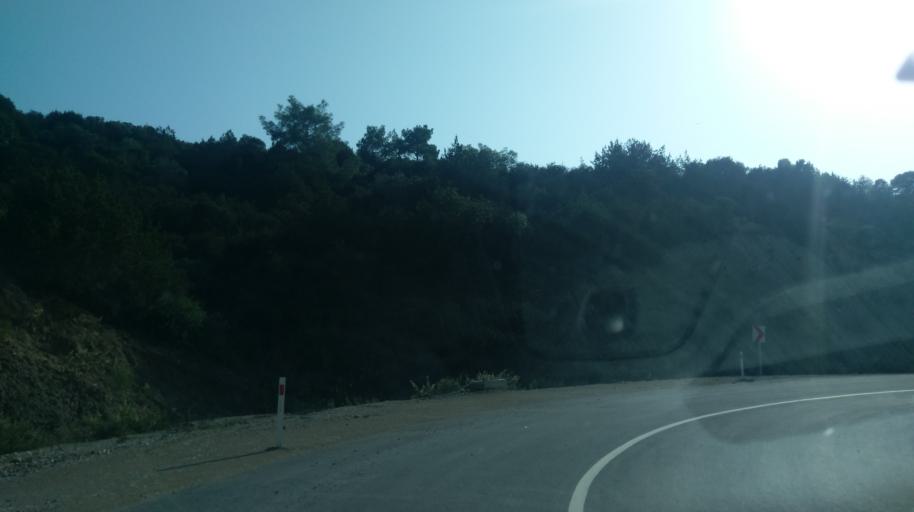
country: CY
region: Ammochostos
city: Leonarisso
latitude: 35.5346
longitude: 34.2500
